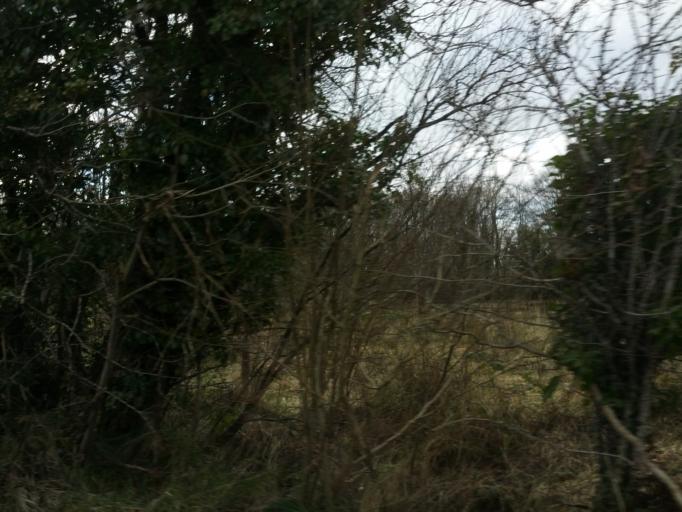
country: IE
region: Connaught
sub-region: County Galway
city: Athenry
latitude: 53.4355
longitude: -8.6743
